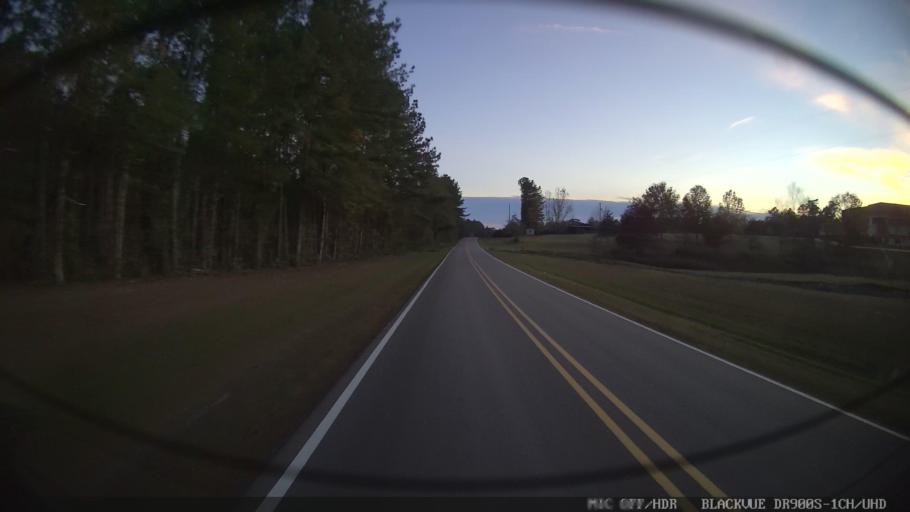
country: US
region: Mississippi
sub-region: Perry County
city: New Augusta
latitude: 31.0702
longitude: -89.1853
